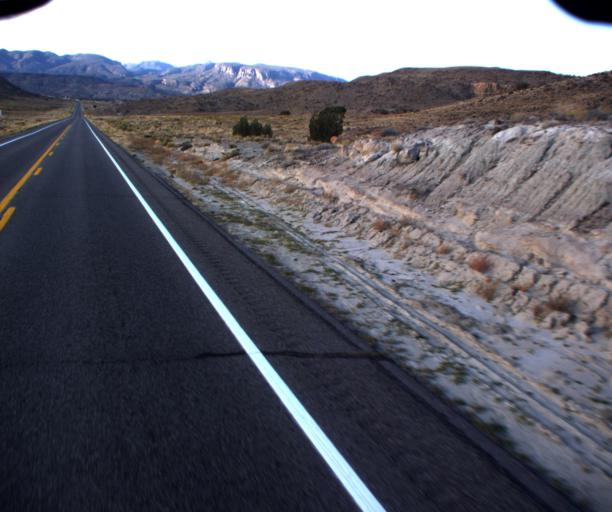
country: US
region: New Mexico
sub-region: San Juan County
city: Shiprock
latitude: 36.9439
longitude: -109.0742
